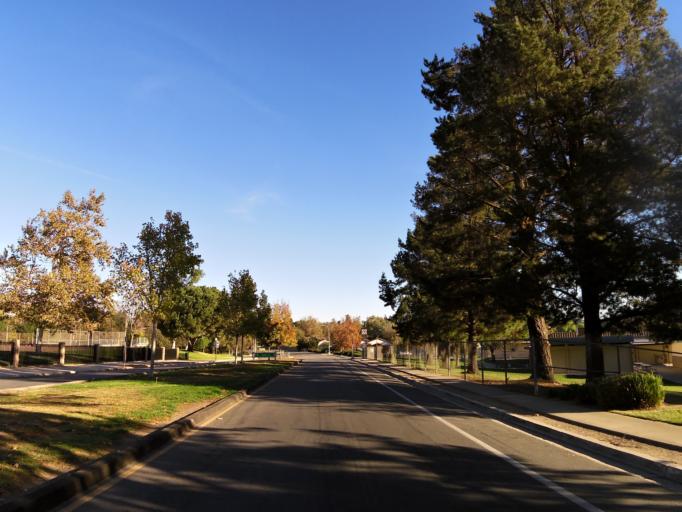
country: US
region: California
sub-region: Ventura County
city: Casa Conejo
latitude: 34.2168
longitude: -118.8934
